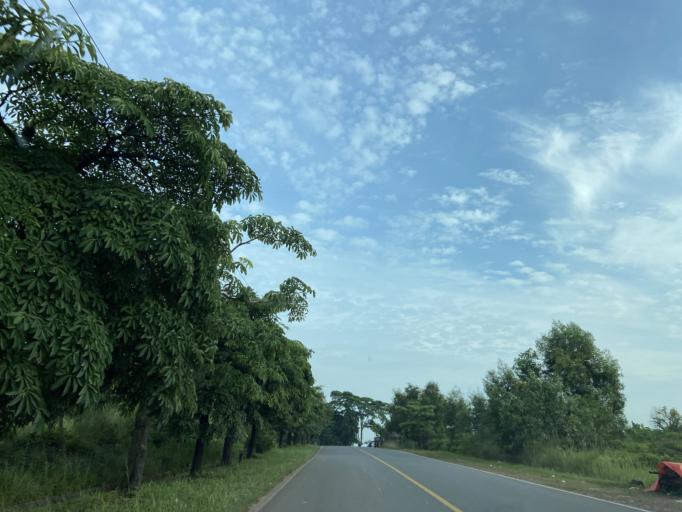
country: ID
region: Riau Islands
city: Tanjungpinang
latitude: 0.9262
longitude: 104.1153
